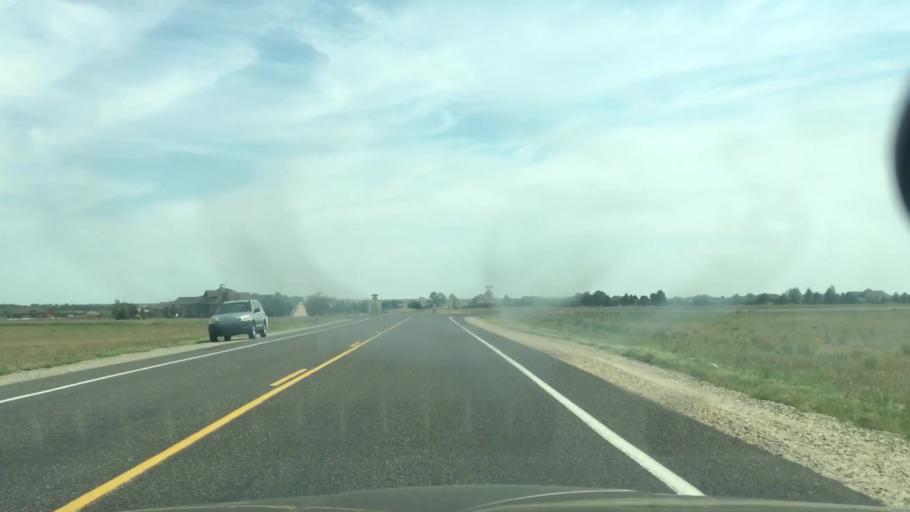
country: US
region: Colorado
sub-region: Larimer County
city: Berthoud
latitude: 40.3345
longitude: -105.1516
